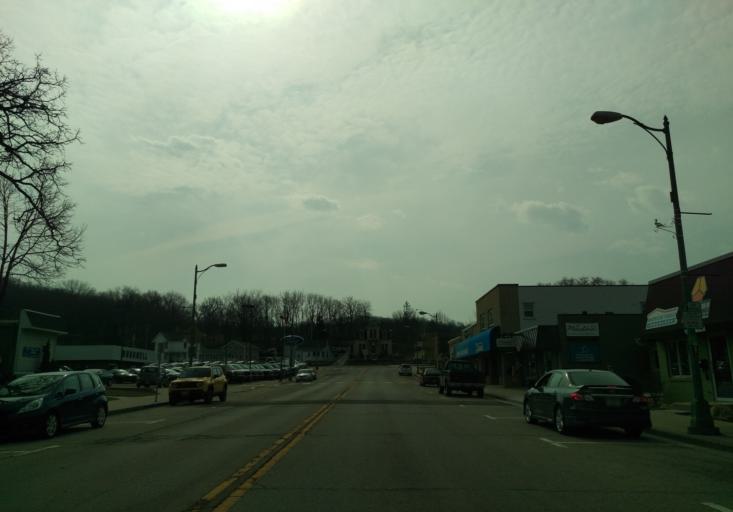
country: US
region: Wisconsin
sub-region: Columbia County
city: Lodi
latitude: 43.3129
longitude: -89.5259
